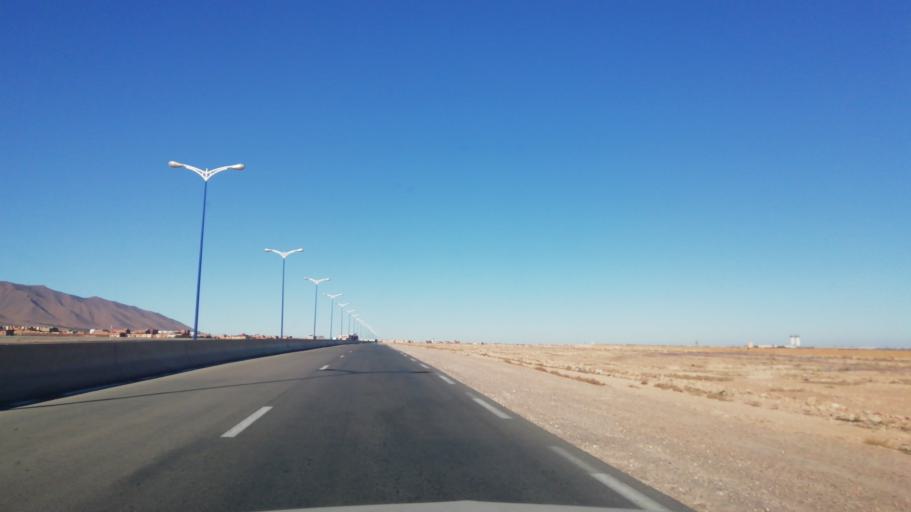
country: DZ
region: Wilaya de Naama
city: Naama
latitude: 33.5205
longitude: -0.2759
